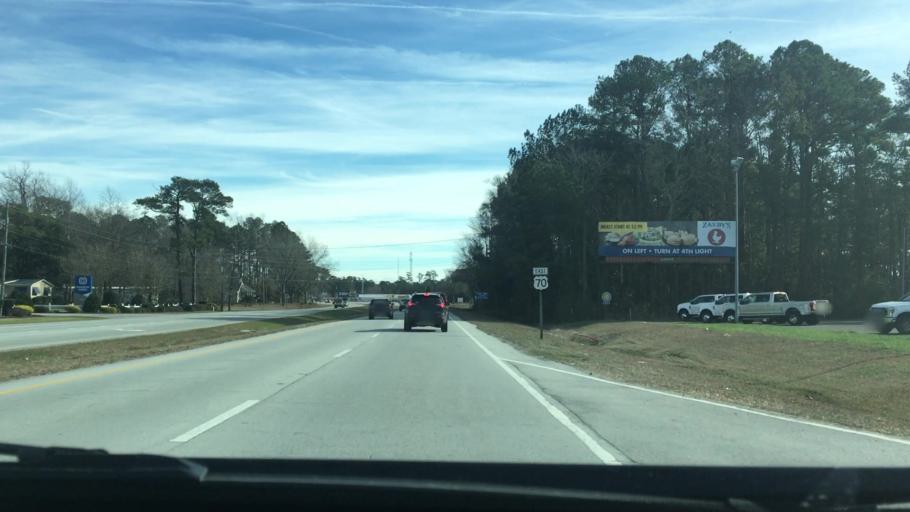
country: US
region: North Carolina
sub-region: Carteret County
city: Newport
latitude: 34.7474
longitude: -76.8353
